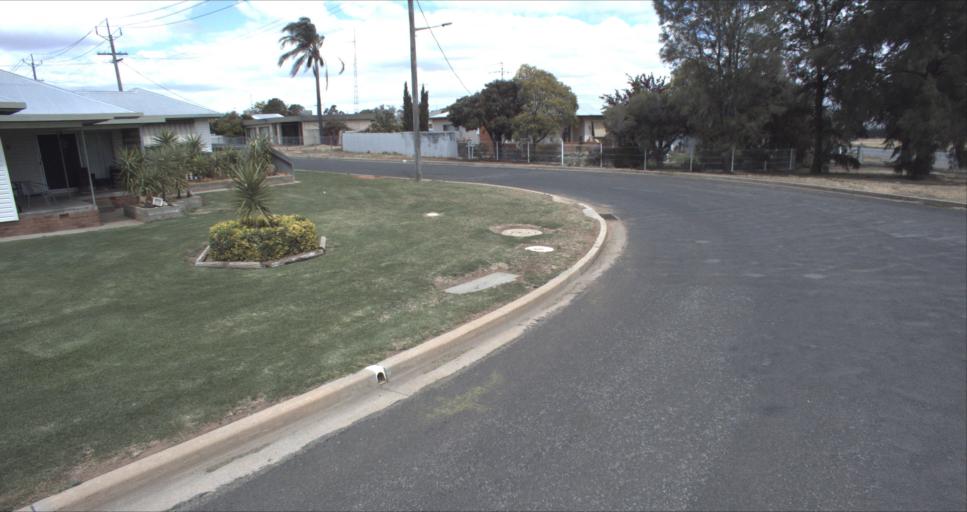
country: AU
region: New South Wales
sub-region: Leeton
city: Leeton
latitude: -34.5618
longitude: 146.3931
